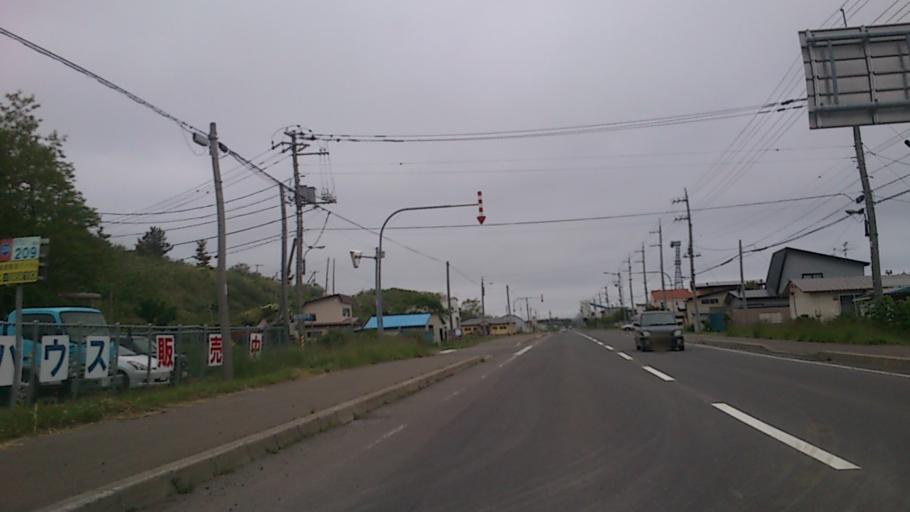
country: JP
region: Hokkaido
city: Iwanai
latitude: 42.4449
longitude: 139.8546
